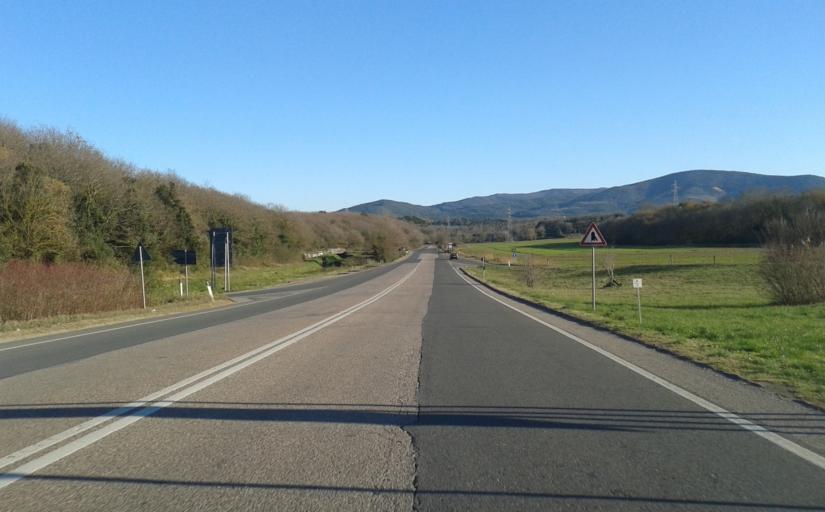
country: IT
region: Tuscany
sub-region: Provincia di Livorno
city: Livorno
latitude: 43.5722
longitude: 10.3508
